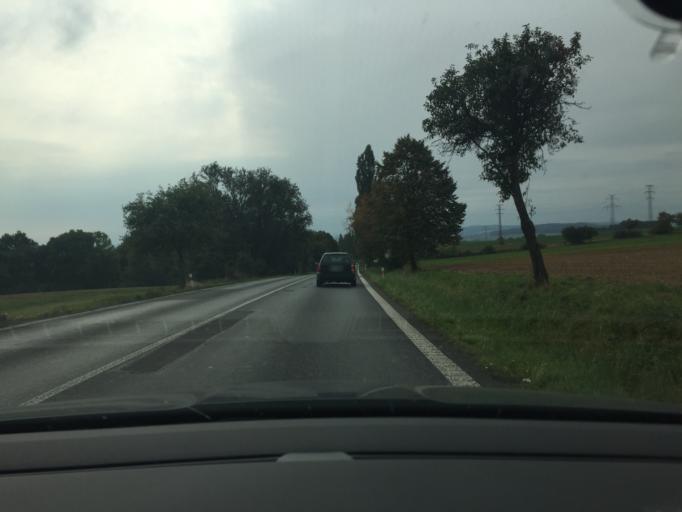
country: CZ
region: Jihocesky
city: Mirovice
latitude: 49.5518
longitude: 14.0827
